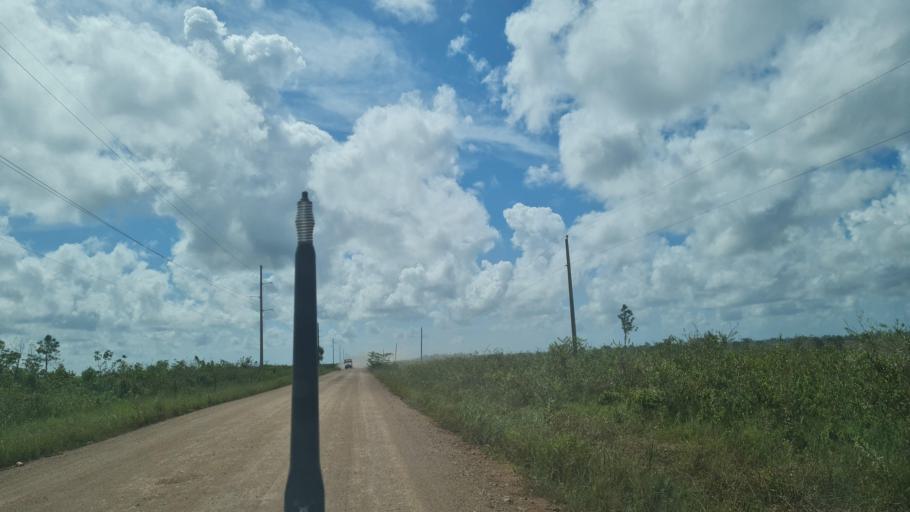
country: NI
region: Atlantico Norte (RAAN)
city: Puerto Cabezas
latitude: 14.1100
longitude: -83.6041
